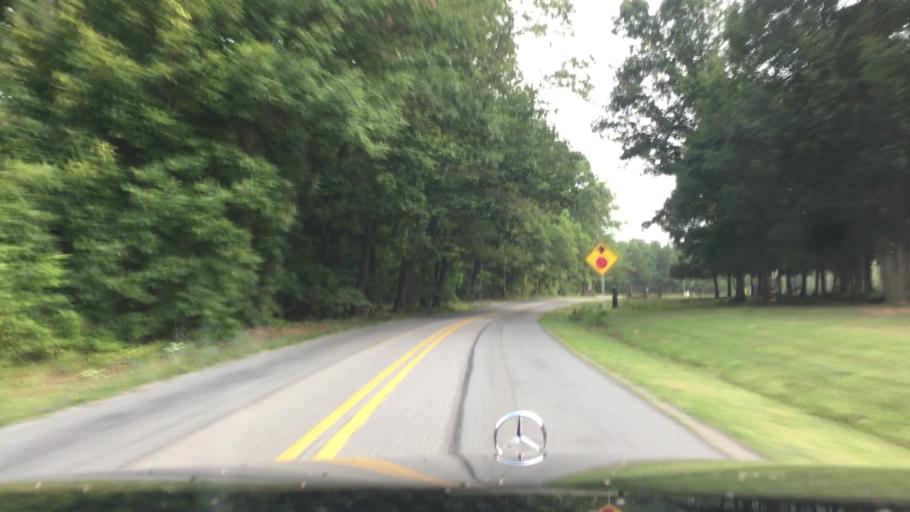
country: US
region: Virginia
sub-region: Campbell County
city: Timberlake
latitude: 37.2835
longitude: -79.3195
